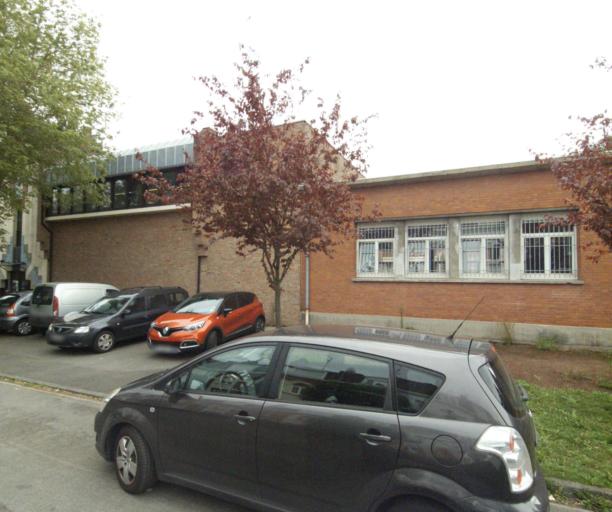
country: FR
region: Nord-Pas-de-Calais
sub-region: Departement du Nord
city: Lambersart
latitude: 50.6455
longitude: 3.0299
